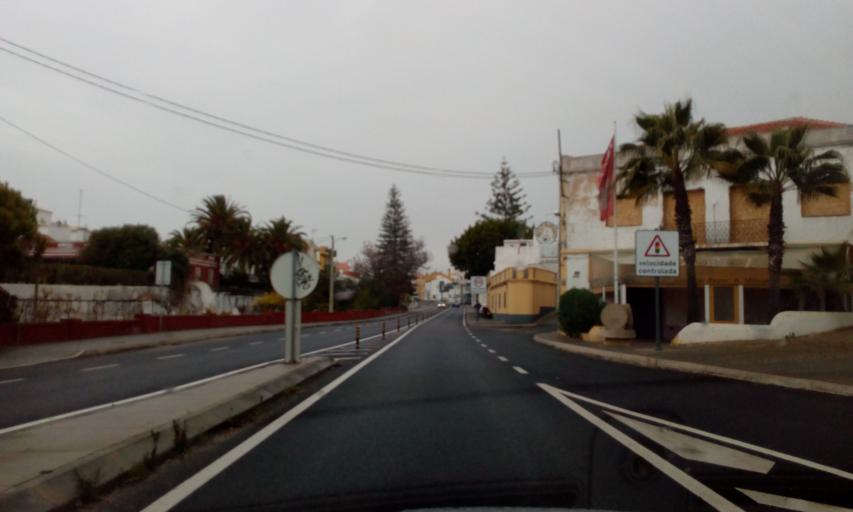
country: PT
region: Faro
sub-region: Silves
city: Armacao de Pera
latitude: 37.1269
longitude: -8.3461
